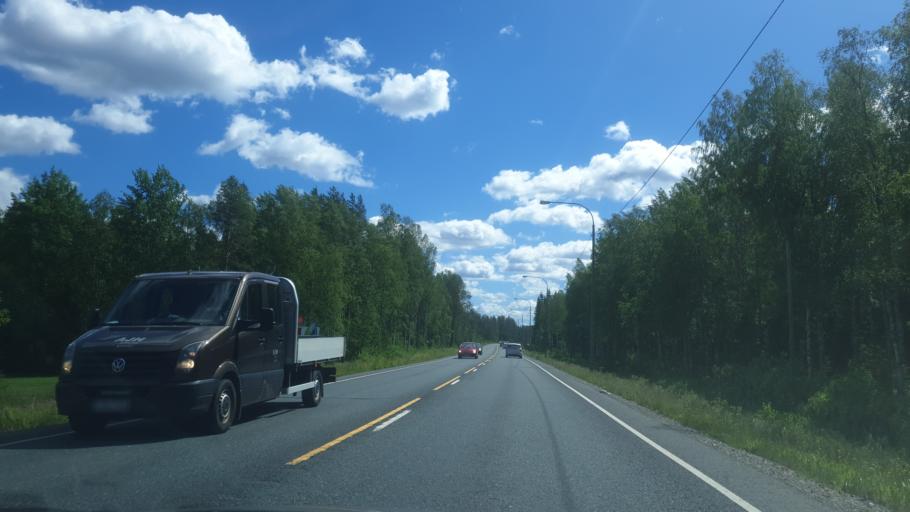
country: FI
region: Northern Savo
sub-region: Varkaus
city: Leppaevirta
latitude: 62.5393
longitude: 27.6367
